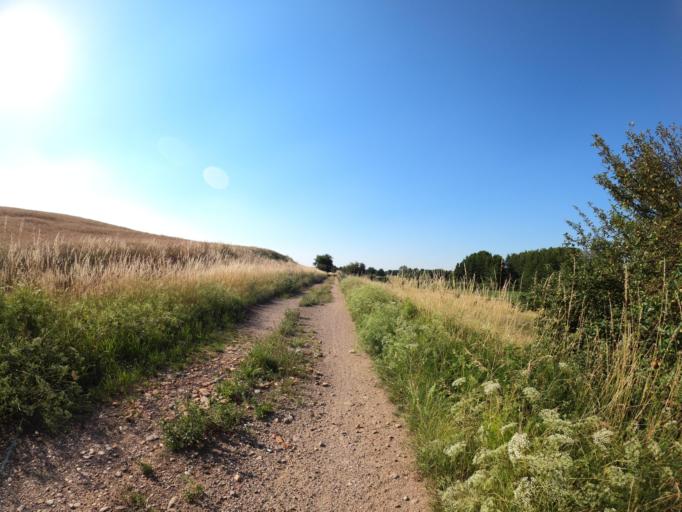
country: DE
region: Brandenburg
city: Gartz
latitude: 53.2236
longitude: 14.3713
